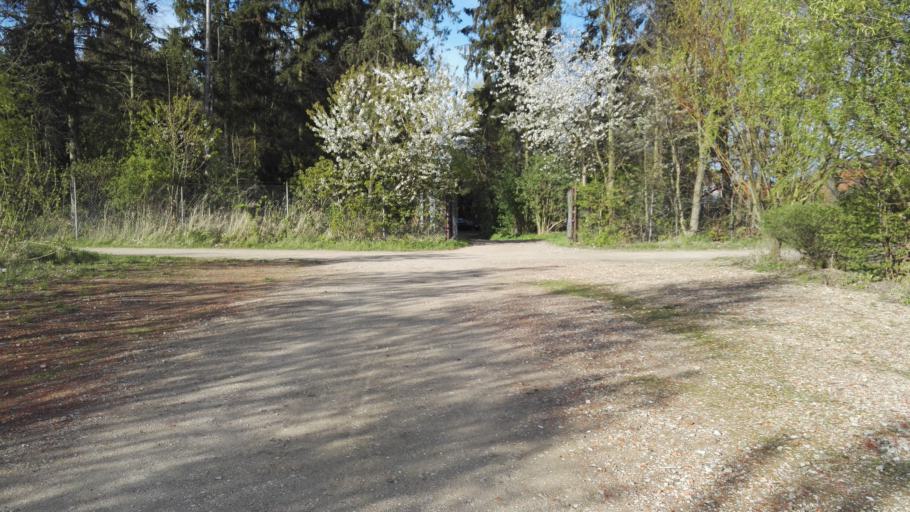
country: DE
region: Lower Saxony
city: Holle
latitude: 52.0712
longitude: 10.1379
